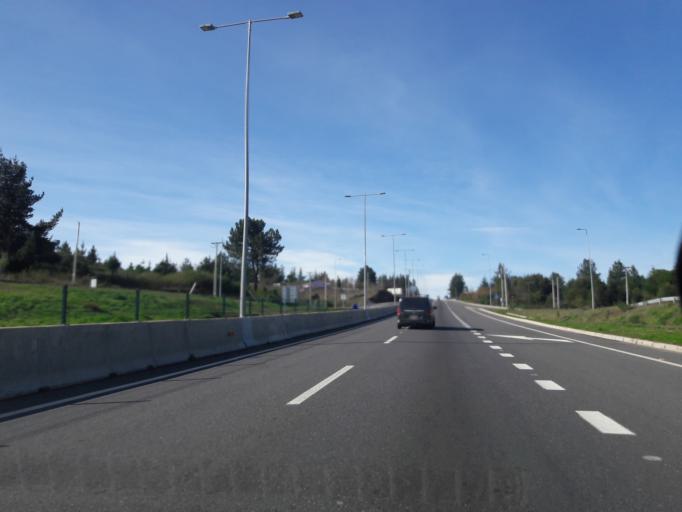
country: CL
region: Biobio
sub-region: Provincia de Biobio
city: Yumbel
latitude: -36.9619
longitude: -72.7193
